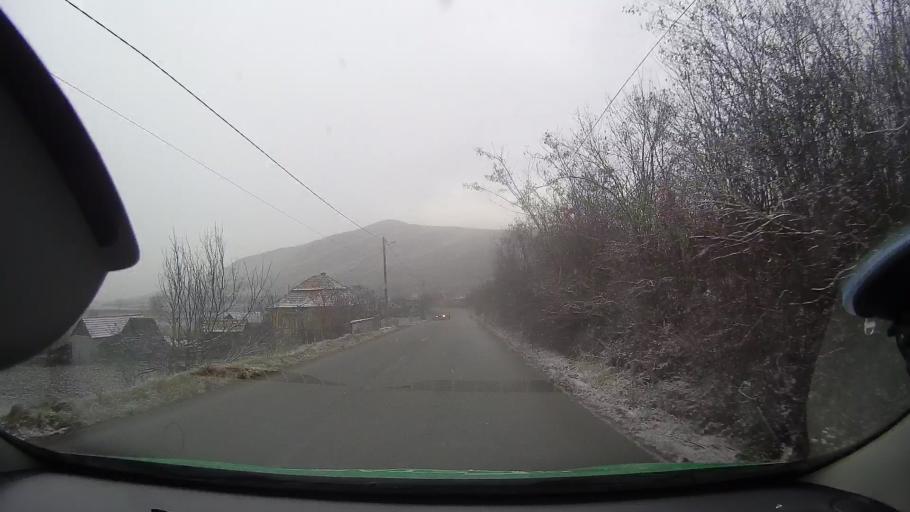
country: RO
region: Alba
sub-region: Comuna Noslac
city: Noslac
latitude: 46.3644
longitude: 23.9317
